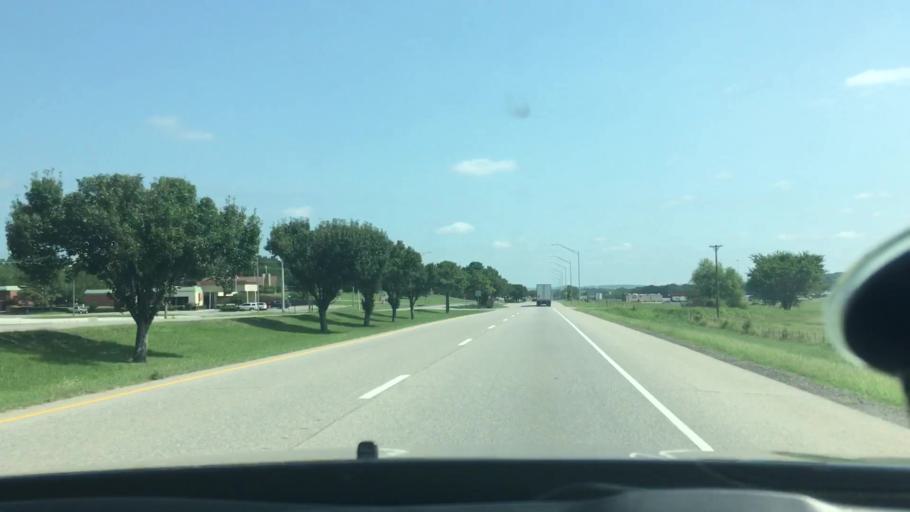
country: US
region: Oklahoma
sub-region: Atoka County
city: Atoka
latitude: 34.3591
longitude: -96.1453
